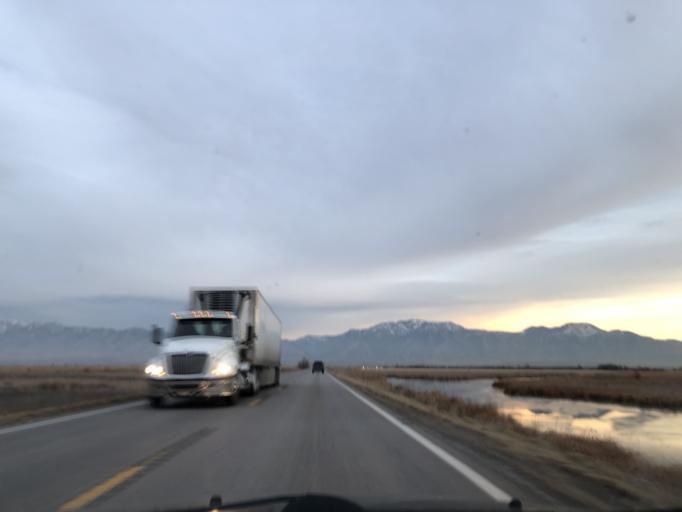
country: US
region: Utah
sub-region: Cache County
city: Benson
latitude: 41.7459
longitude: -111.9426
